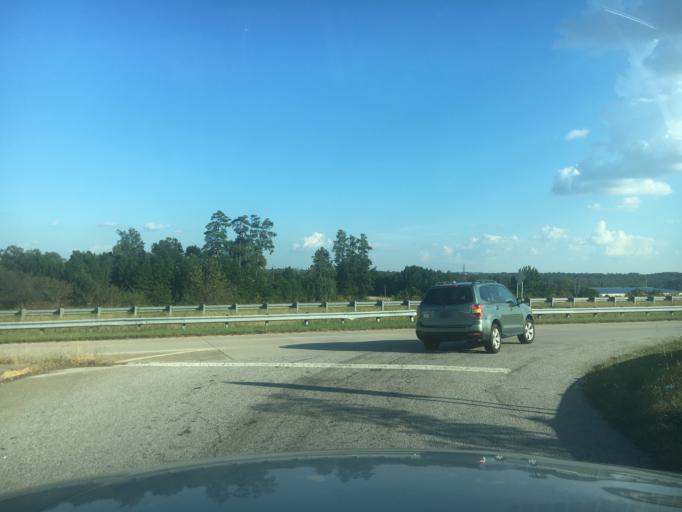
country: US
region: South Carolina
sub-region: Greenville County
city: Greer
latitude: 34.9374
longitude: -82.1909
